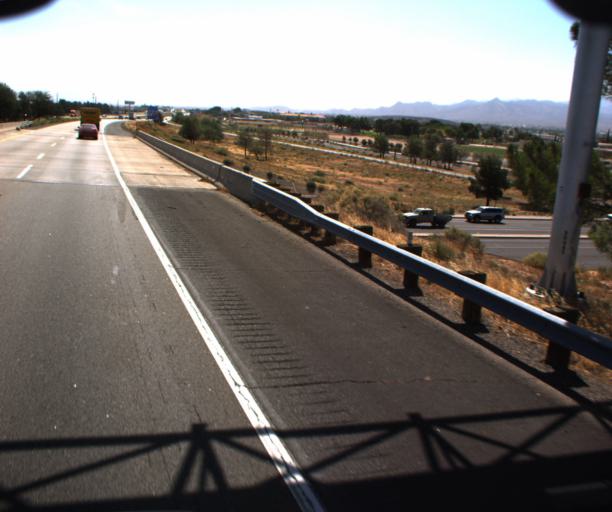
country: US
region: Arizona
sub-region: Mohave County
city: Kingman
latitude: 35.2170
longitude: -114.0360
